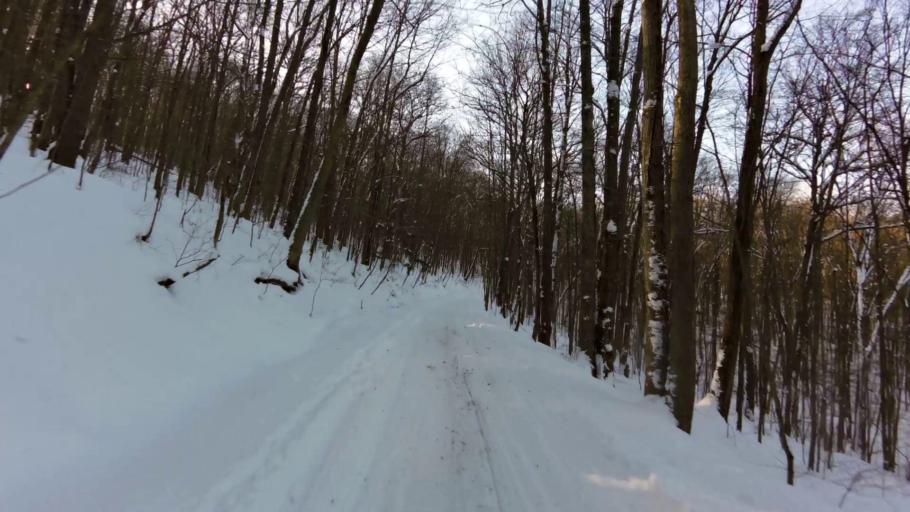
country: US
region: Pennsylvania
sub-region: McKean County
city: Foster Brook
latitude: 42.0642
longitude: -78.6536
